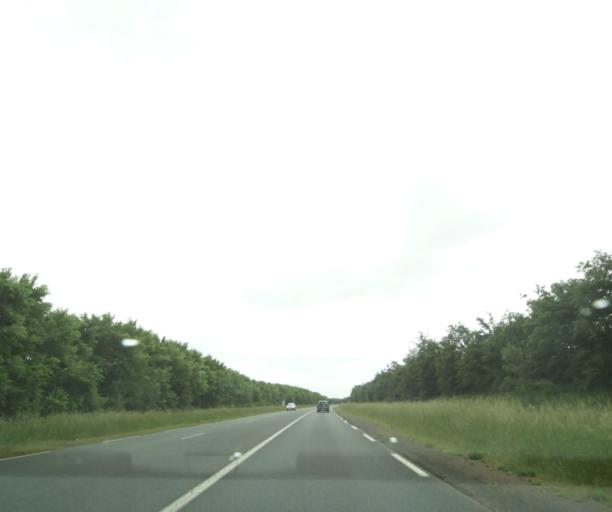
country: FR
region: Poitou-Charentes
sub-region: Departement des Deux-Sevres
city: Airvault
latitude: 46.8146
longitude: -0.2086
